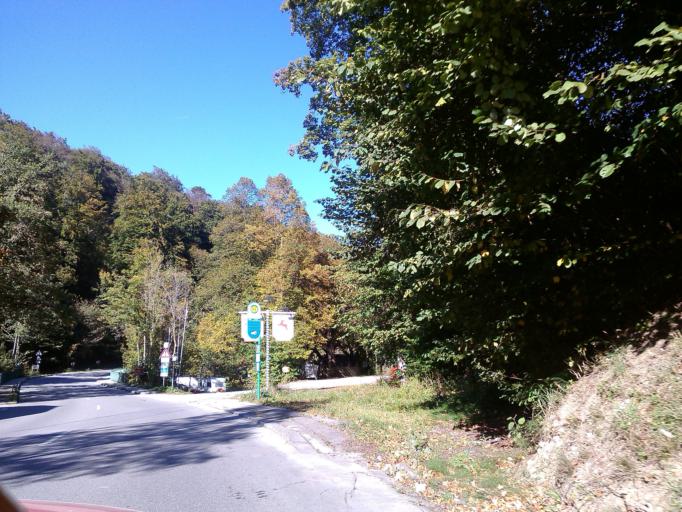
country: DE
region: Bavaria
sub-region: Upper Bavaria
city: Starnberg
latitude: 48.0347
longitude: 11.3589
